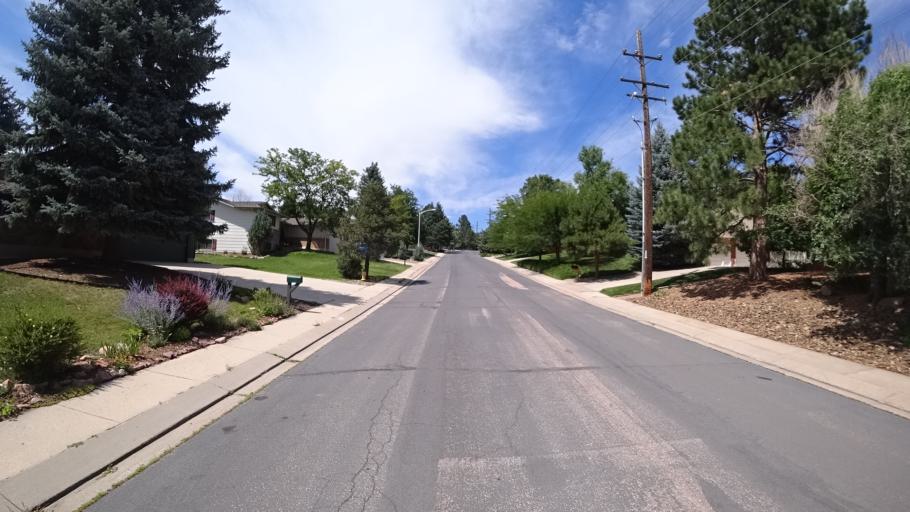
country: US
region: Colorado
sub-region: El Paso County
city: Air Force Academy
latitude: 38.9314
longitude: -104.8292
